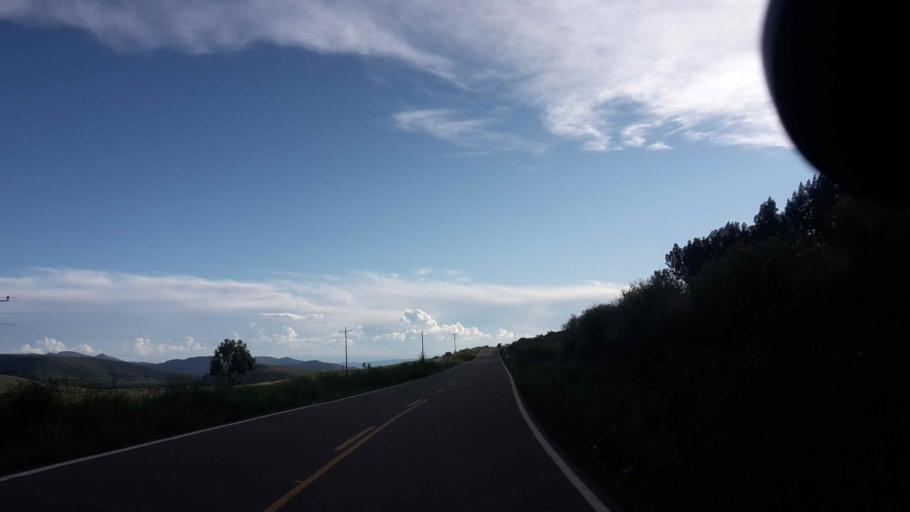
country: BO
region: Cochabamba
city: Arani
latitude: -17.5556
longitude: -65.6975
